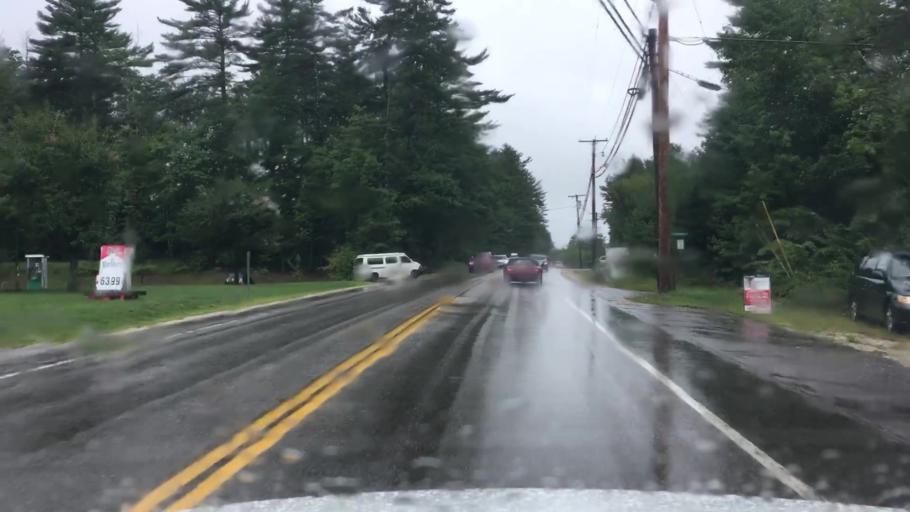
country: US
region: New Hampshire
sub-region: Carroll County
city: Conway
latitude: 43.9958
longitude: -71.0656
